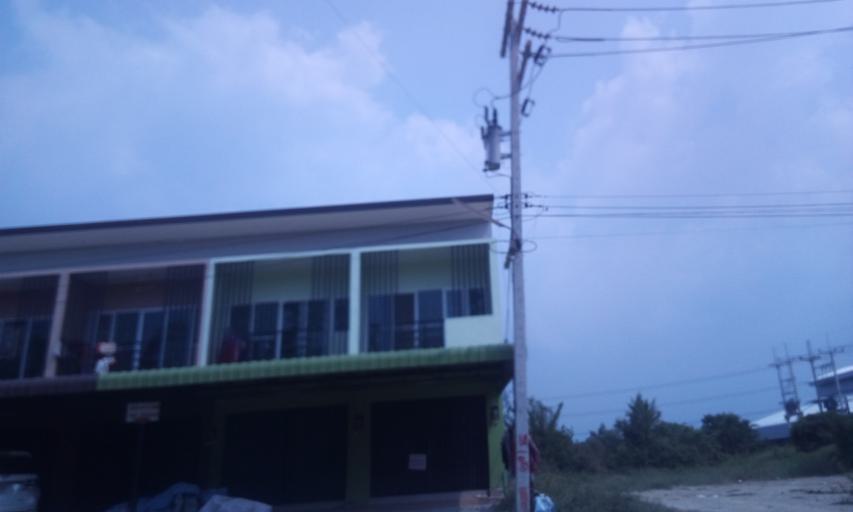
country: TH
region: Chon Buri
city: Ban Bueng
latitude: 13.3445
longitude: 101.1932
